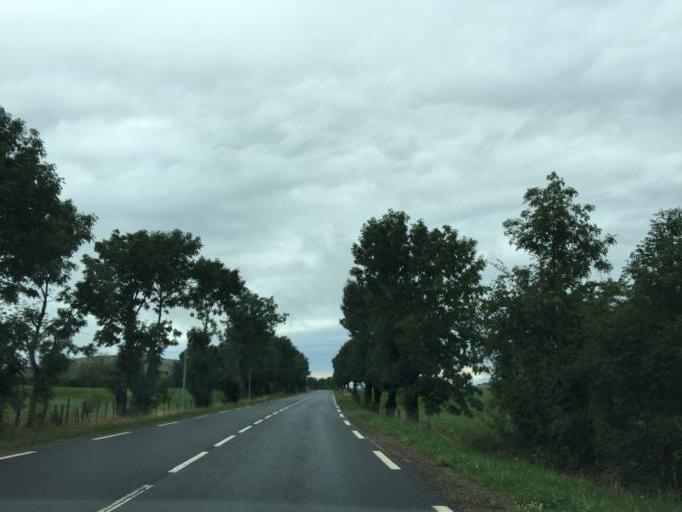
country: FR
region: Midi-Pyrenees
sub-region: Departement de l'Aveyron
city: Laguiole
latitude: 44.6354
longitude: 2.8306
